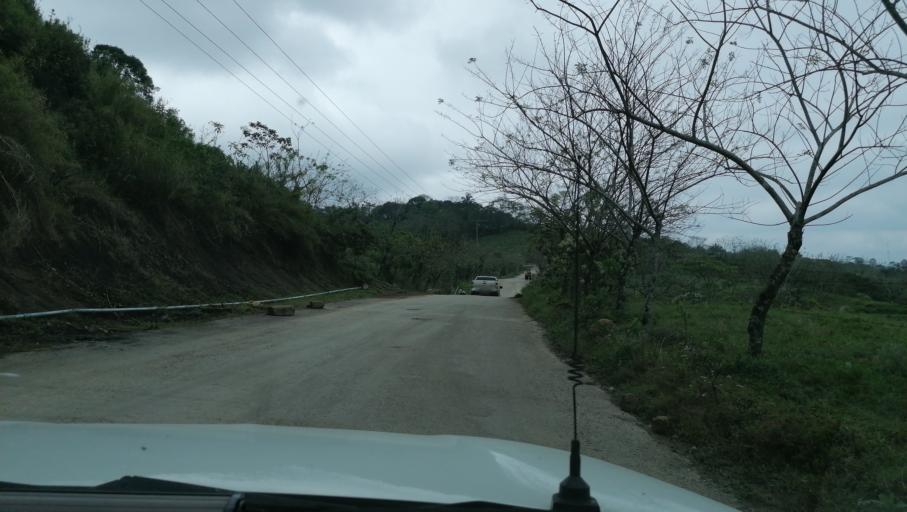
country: MX
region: Chiapas
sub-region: Francisco Leon
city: San Miguel la Sardina
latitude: 17.2796
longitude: -93.2751
